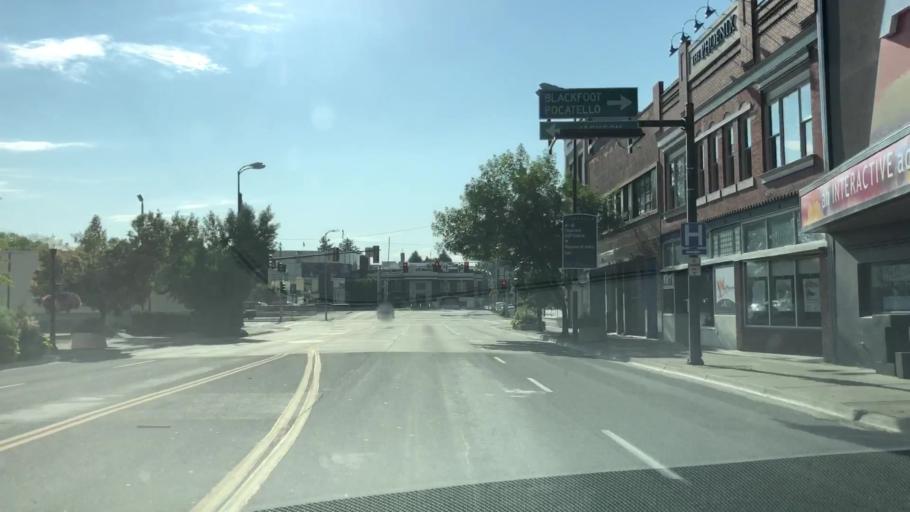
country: US
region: Idaho
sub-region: Bonneville County
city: Idaho Falls
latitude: 43.4913
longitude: -112.0401
